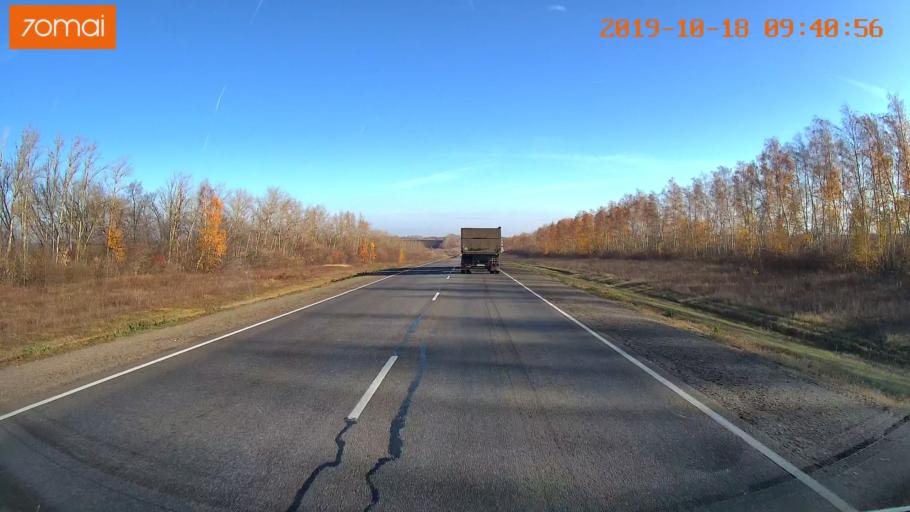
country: RU
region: Tula
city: Kazachka
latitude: 53.2694
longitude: 38.1554
